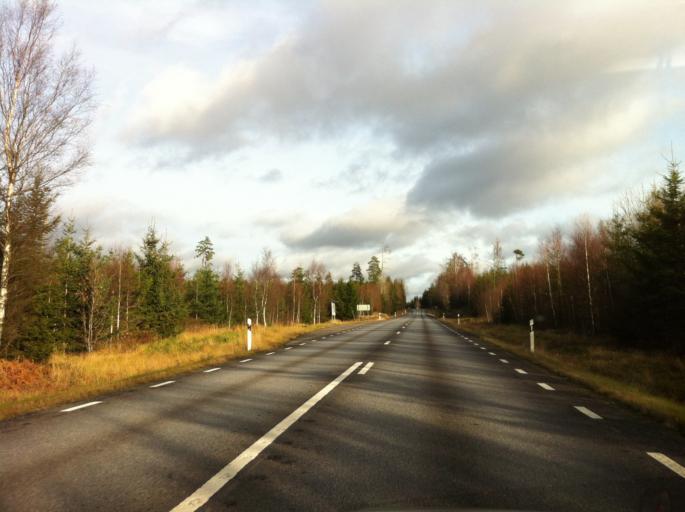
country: SE
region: Kronoberg
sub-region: Alvesta Kommun
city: Vislanda
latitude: 56.7436
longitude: 14.5096
